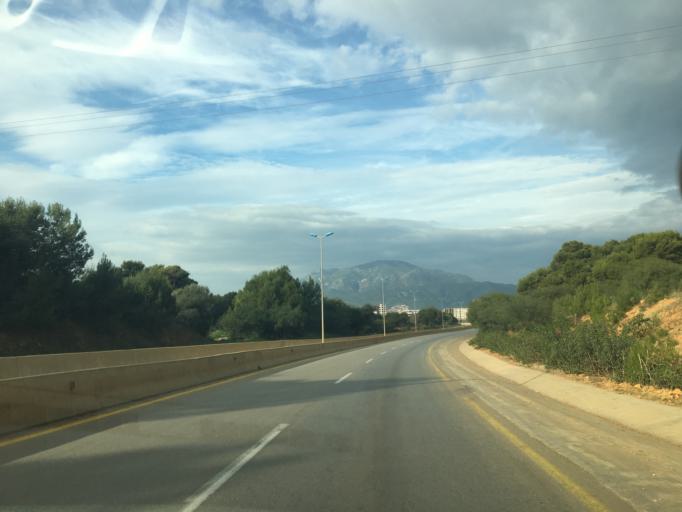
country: DZ
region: Tipaza
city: Tipasa
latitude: 36.5823
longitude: 2.4809
